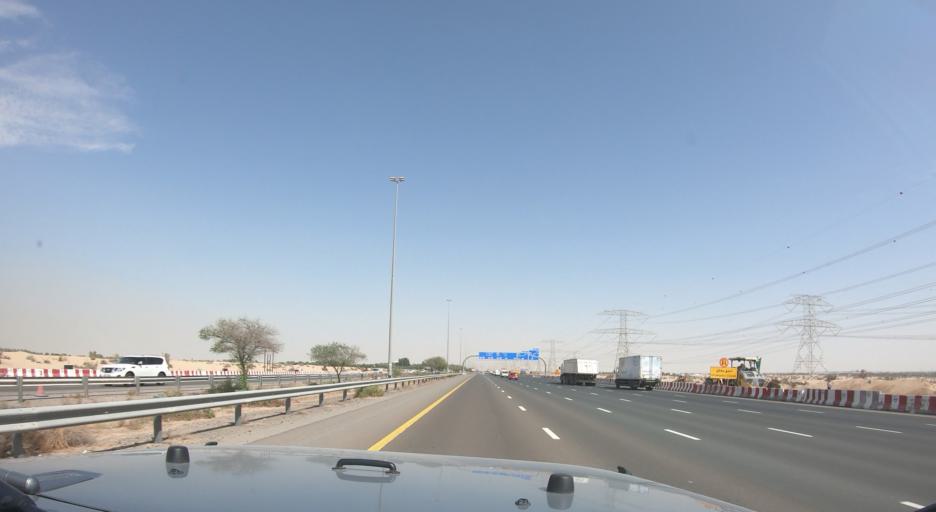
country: AE
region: Ash Shariqah
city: Sharjah
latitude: 25.1820
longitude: 55.5208
